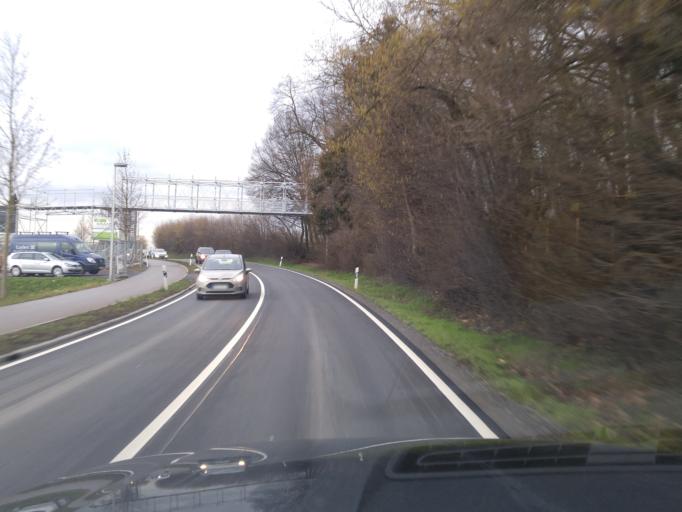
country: DE
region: Baden-Wuerttemberg
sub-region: Regierungsbezirk Stuttgart
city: Ohringen
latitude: 49.2000
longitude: 9.5237
